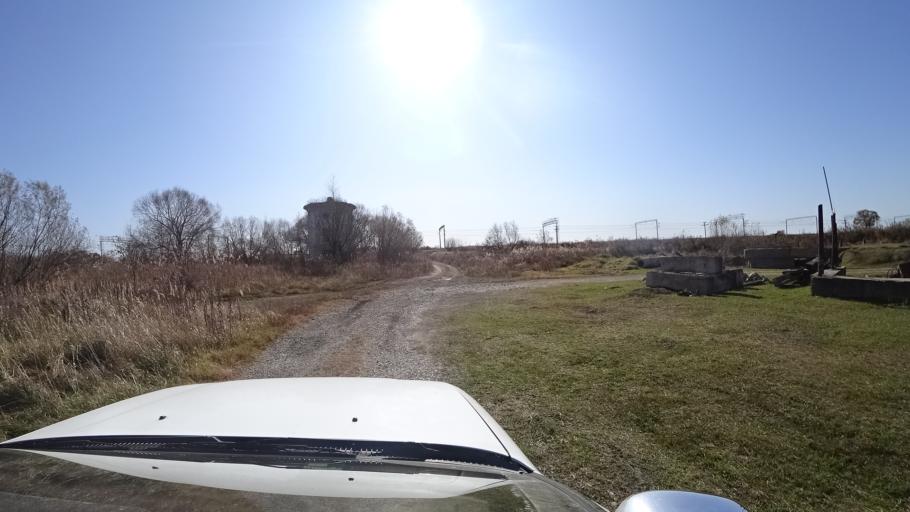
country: RU
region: Primorskiy
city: Dal'nerechensk
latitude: 45.9114
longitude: 133.7898
